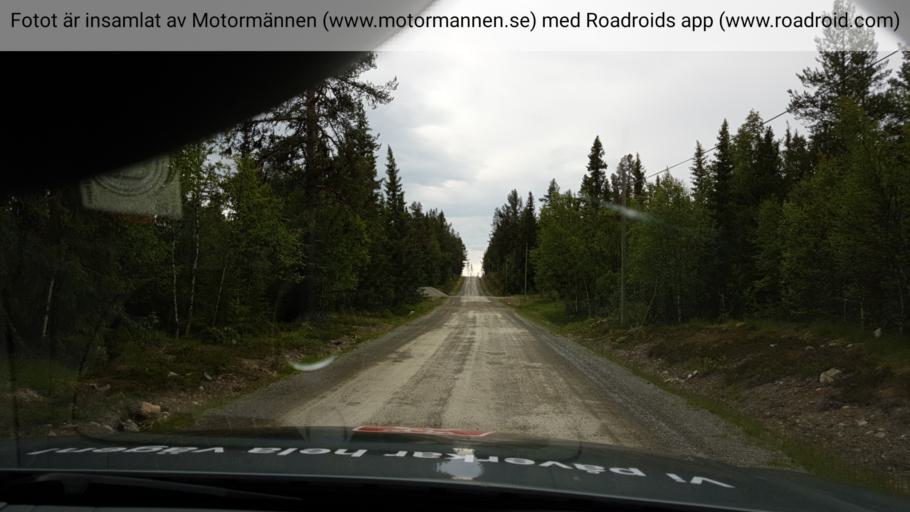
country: SE
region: Jaemtland
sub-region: Are Kommun
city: Jarpen
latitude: 62.8187
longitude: 13.8090
